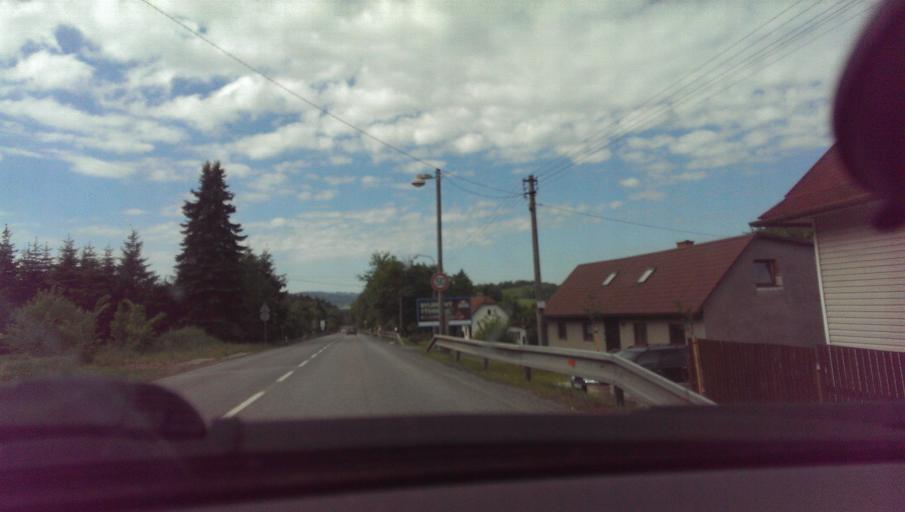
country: CZ
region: Zlin
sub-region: Okres Vsetin
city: Roznov pod Radhostem
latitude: 49.4817
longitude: 18.1687
